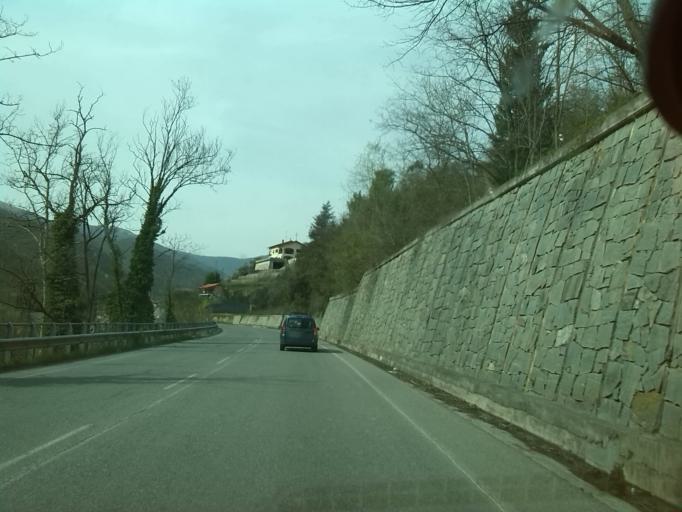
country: IT
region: Liguria
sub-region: Provincia di Imperia
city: Vessalico
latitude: 44.0499
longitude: 7.9689
